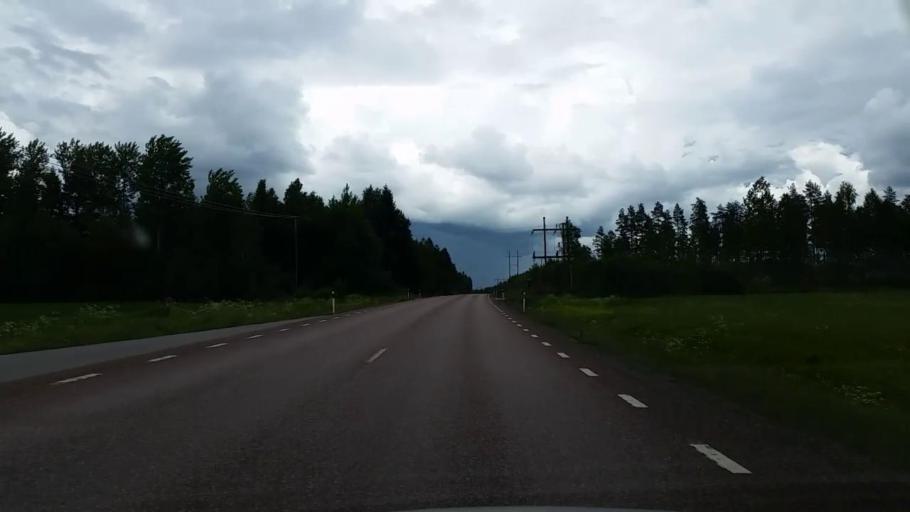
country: SE
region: Gaevleborg
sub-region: Hofors Kommun
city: Hofors
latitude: 60.5176
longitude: 16.4399
